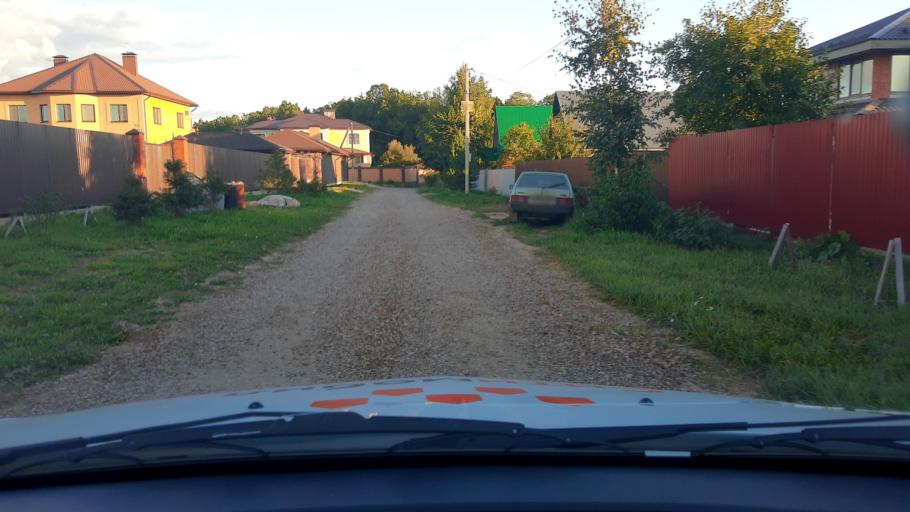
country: RU
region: Bashkortostan
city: Ufa
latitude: 54.6544
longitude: 56.0508
